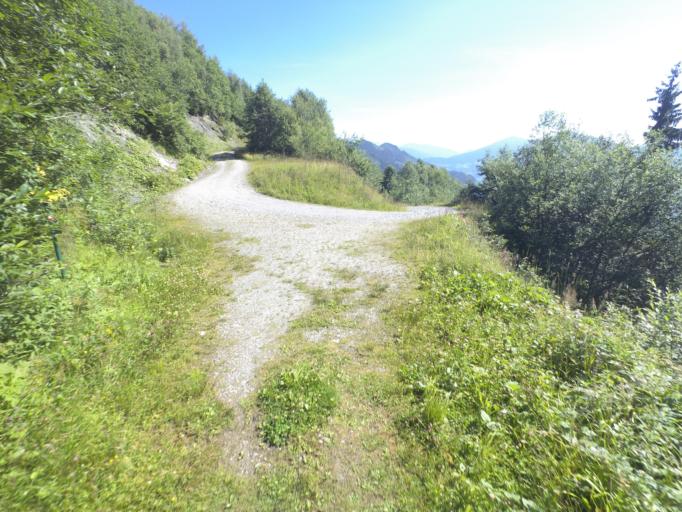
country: AT
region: Salzburg
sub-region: Politischer Bezirk Sankt Johann im Pongau
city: Sankt Veit im Pongau
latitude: 47.3524
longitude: 13.1519
